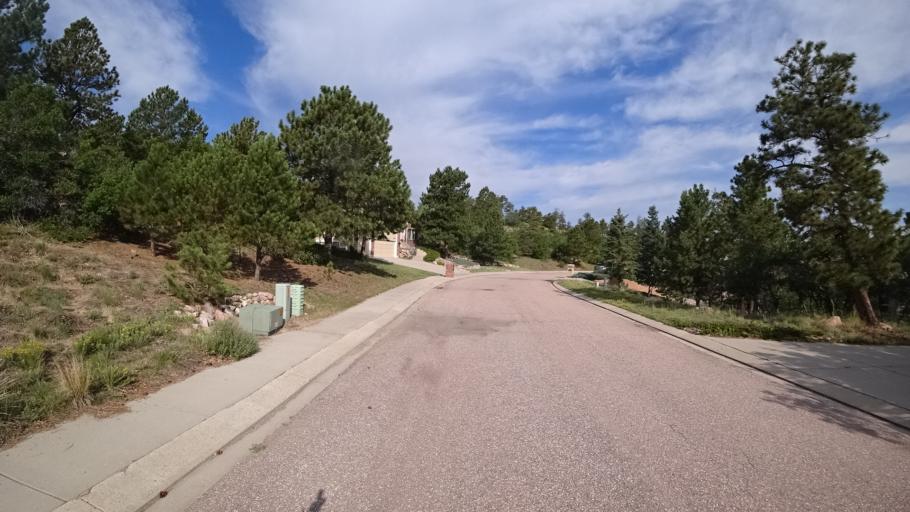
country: US
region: Colorado
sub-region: El Paso County
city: Air Force Academy
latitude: 38.9427
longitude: -104.8304
